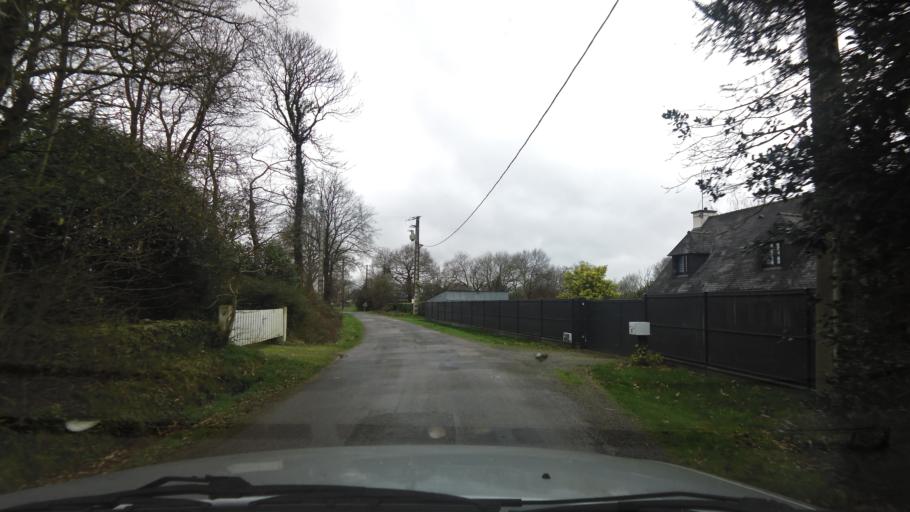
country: FR
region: Brittany
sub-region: Departement du Morbihan
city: Serent
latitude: 47.7778
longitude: -2.4708
